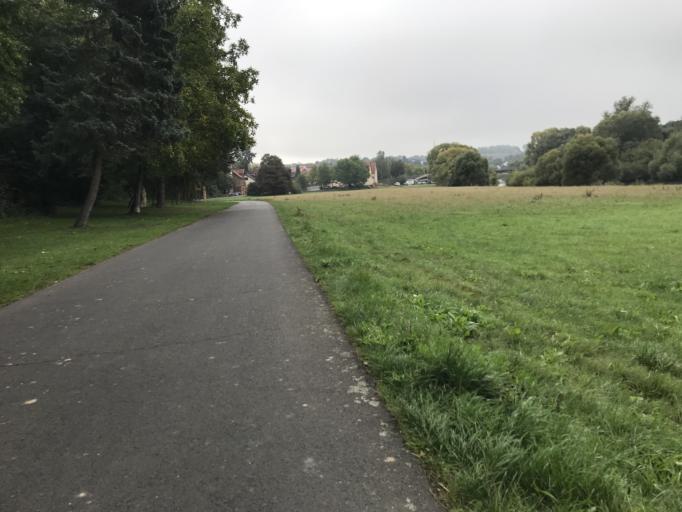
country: DE
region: Hesse
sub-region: Regierungsbezirk Kassel
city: Guxhagen
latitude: 51.2064
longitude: 9.4771
